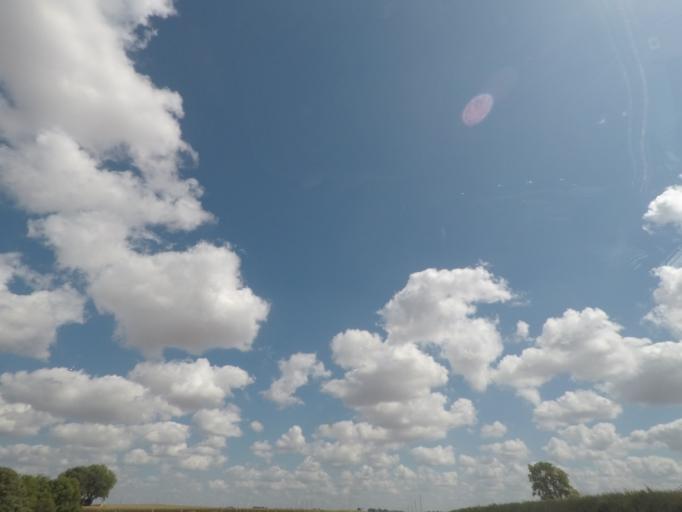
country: US
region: Iowa
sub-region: Story County
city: Nevada
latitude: 42.0776
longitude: -93.3533
